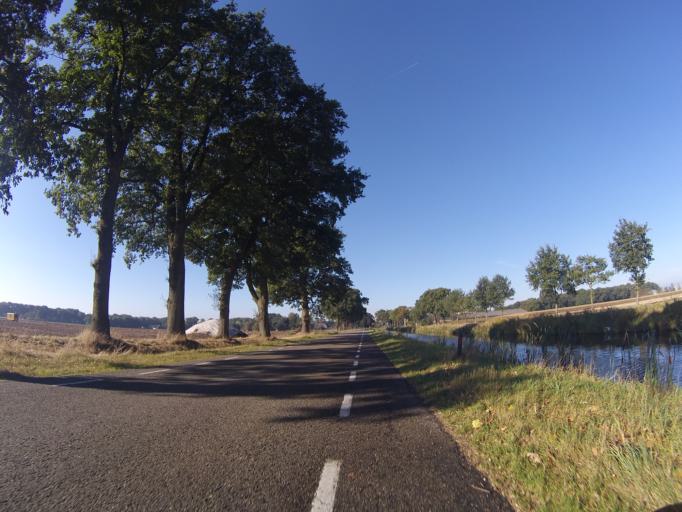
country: NL
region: Drenthe
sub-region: Gemeente Coevorden
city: Dalen
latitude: 52.7300
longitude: 6.6862
